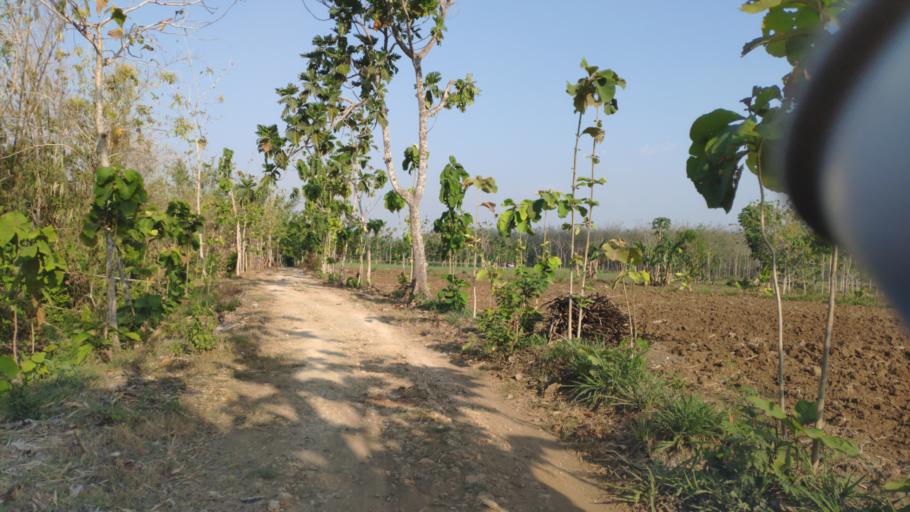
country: ID
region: Central Java
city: Ngapus
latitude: -6.9764
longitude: 111.1907
